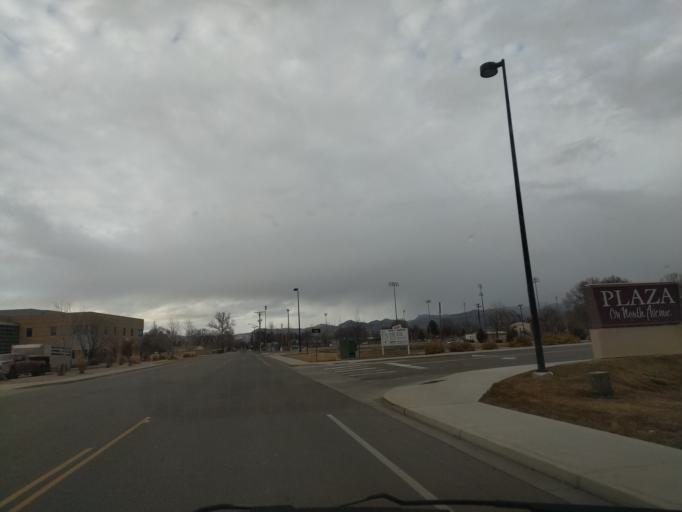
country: US
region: Colorado
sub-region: Mesa County
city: Fruitvale
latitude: 39.0782
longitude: -108.5198
